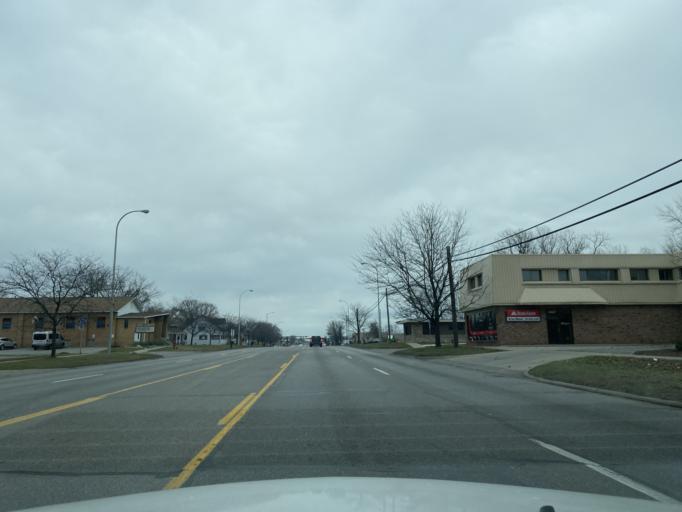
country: US
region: Michigan
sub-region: Wayne County
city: Taylor
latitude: 42.1974
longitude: -83.2720
